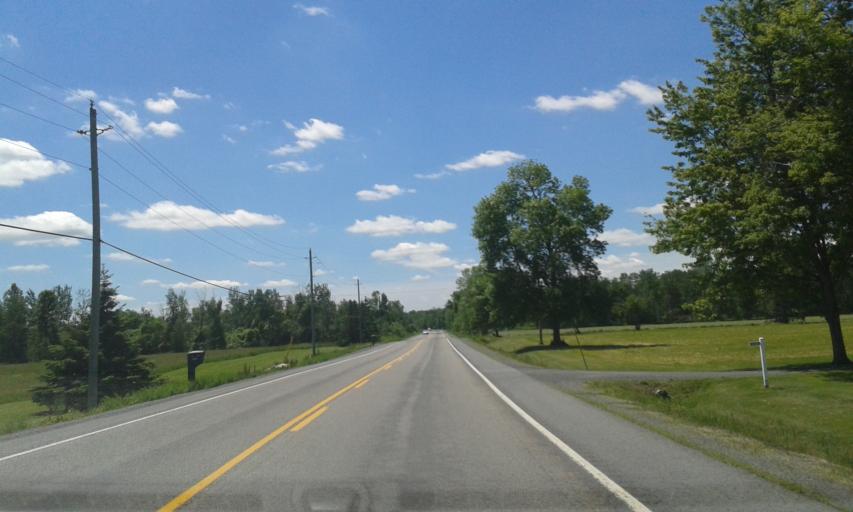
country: CA
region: Ontario
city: Cornwall
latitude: 45.1216
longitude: -74.5077
